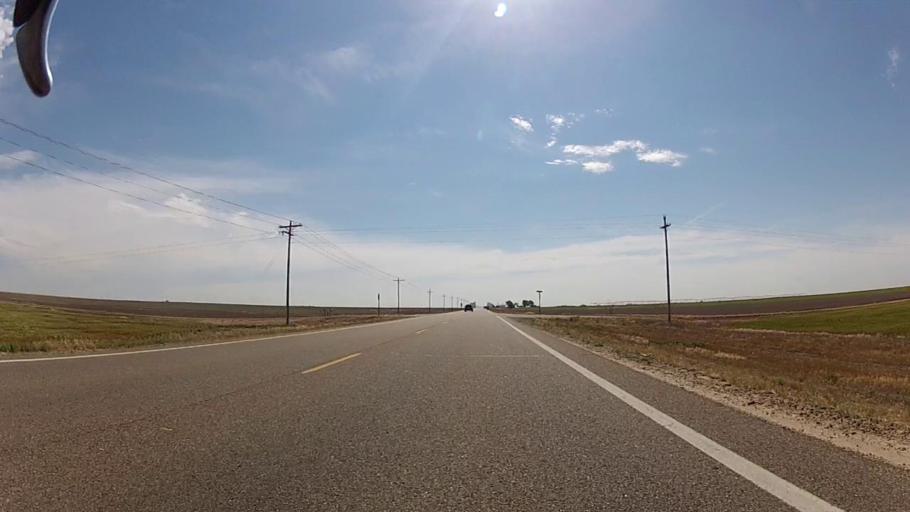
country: US
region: Kansas
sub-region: Grant County
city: Ulysses
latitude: 37.5618
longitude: -101.2729
